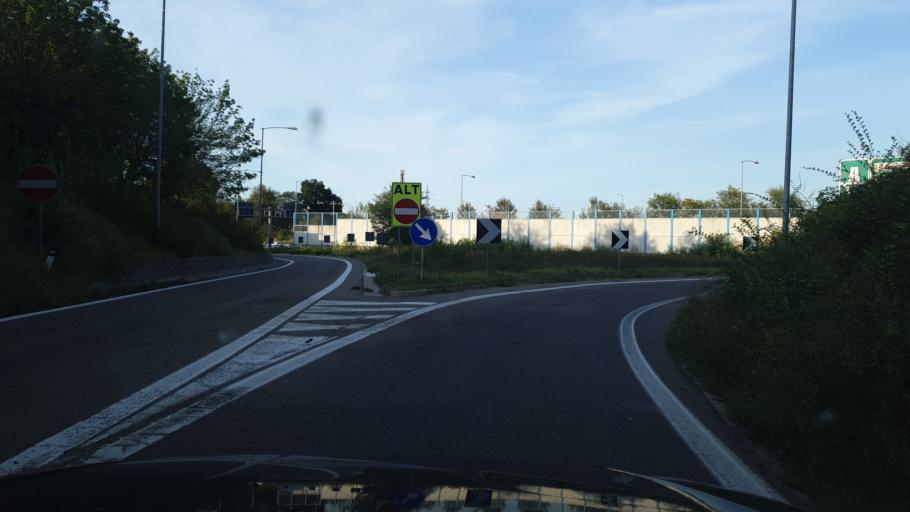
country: IT
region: Emilia-Romagna
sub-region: Provincia di Bologna
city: Quarto Inferiore
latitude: 44.5102
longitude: 11.3792
